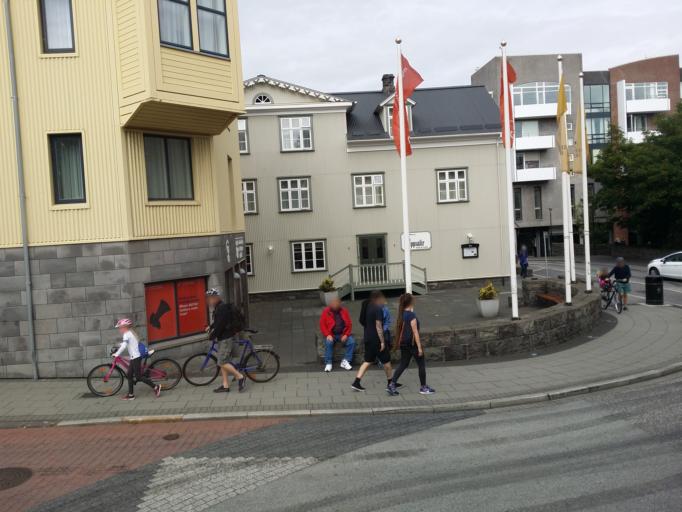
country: IS
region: Capital Region
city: Kopavogur
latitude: 64.1471
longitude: -21.9428
